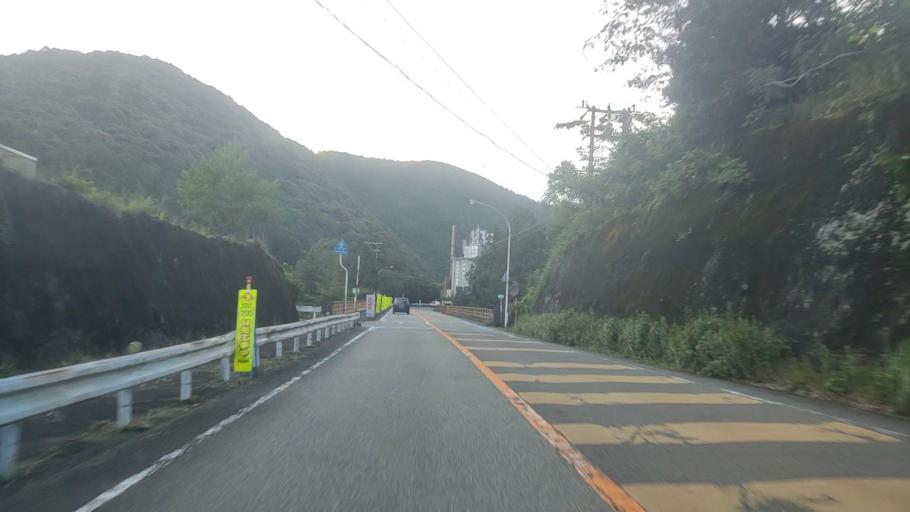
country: JP
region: Wakayama
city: Tanabe
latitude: 33.8154
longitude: 135.5534
